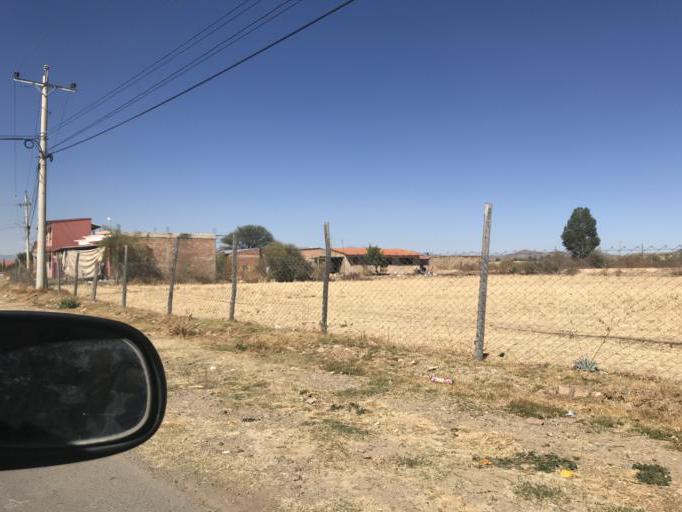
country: BO
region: Cochabamba
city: Tarata
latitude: -17.6023
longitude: -65.9810
